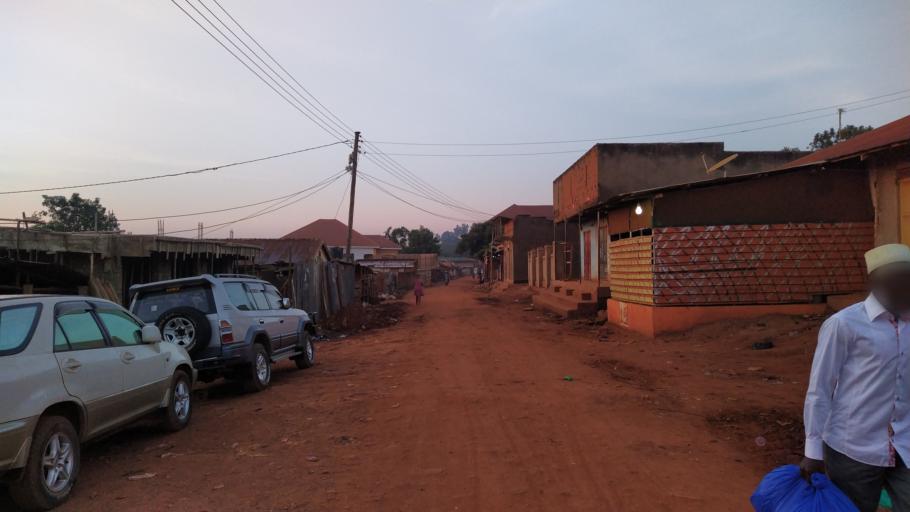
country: UG
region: Central Region
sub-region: Kampala District
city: Kampala
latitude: 0.2746
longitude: 32.5732
